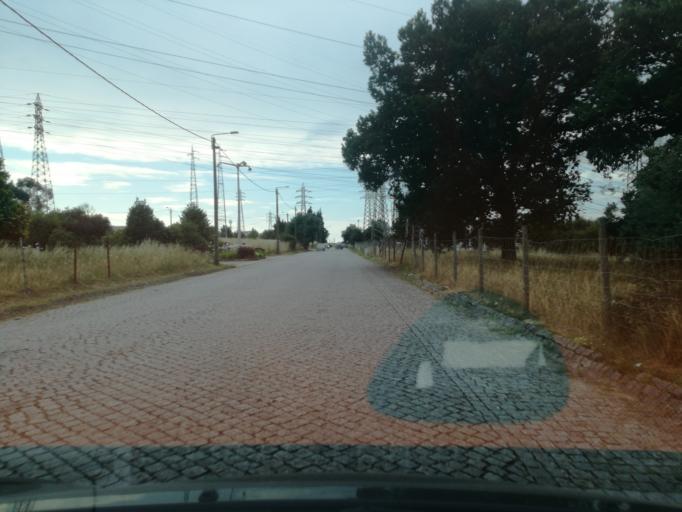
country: PT
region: Porto
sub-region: Maia
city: Maia
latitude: 41.2290
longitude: -8.6061
